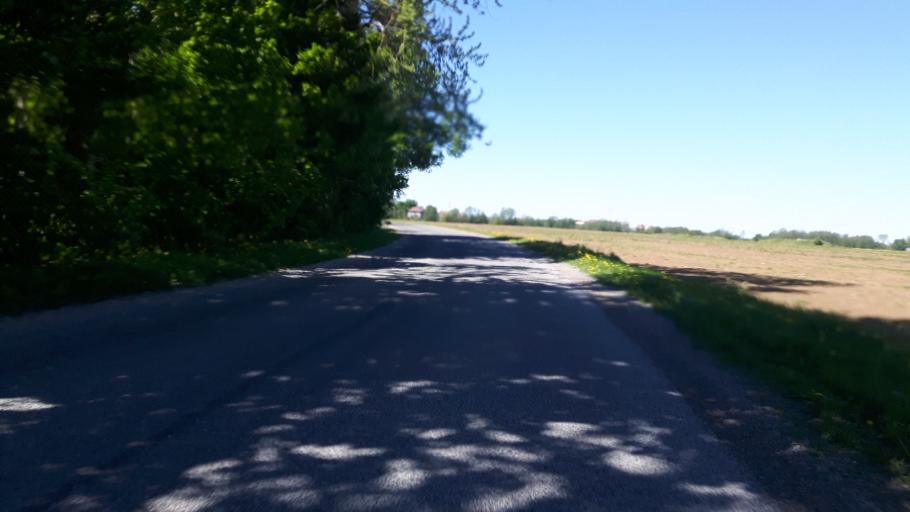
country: EE
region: Ida-Virumaa
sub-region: Sillamaee linn
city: Sillamae
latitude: 59.3818
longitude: 27.8249
